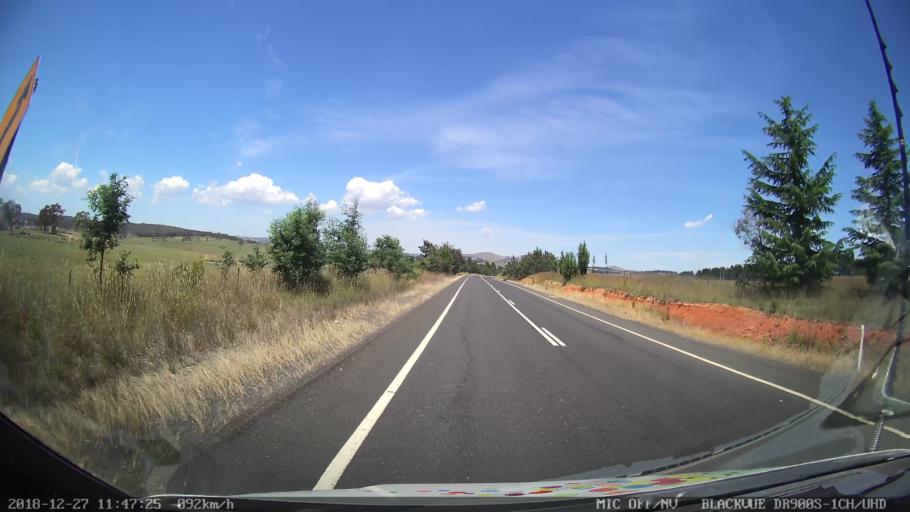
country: AU
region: New South Wales
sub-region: Bathurst Regional
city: Perthville
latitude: -33.5961
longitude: 149.4456
